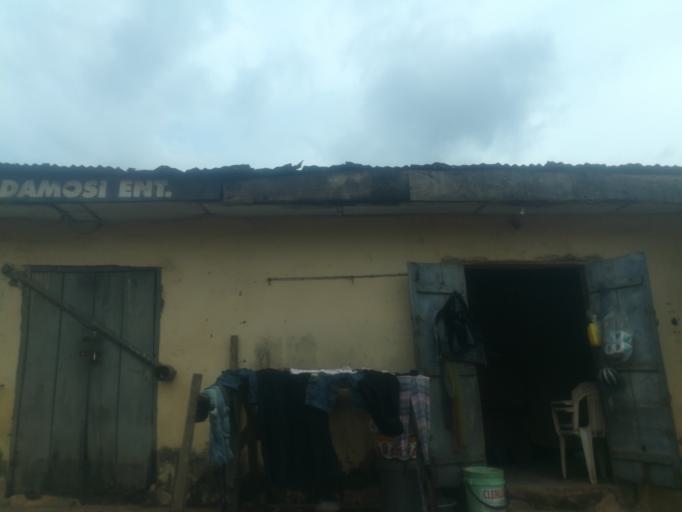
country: NG
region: Oyo
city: Ibadan
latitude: 7.3788
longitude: 3.9625
